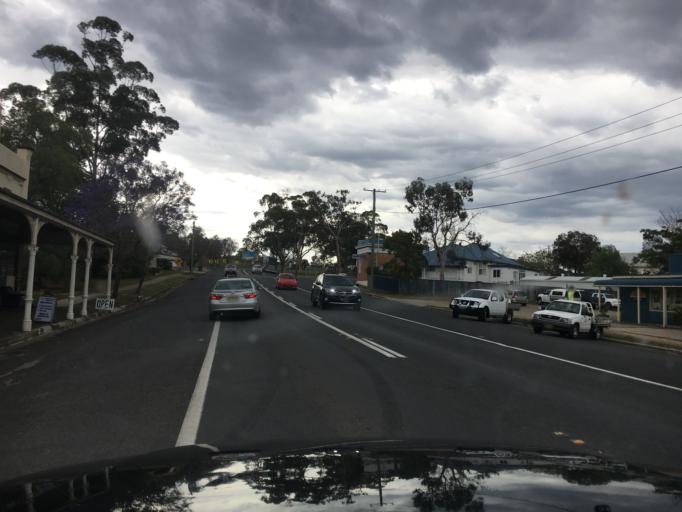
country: AU
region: New South Wales
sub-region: Muswellbrook
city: Muswellbrook
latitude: -32.1616
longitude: 150.8894
